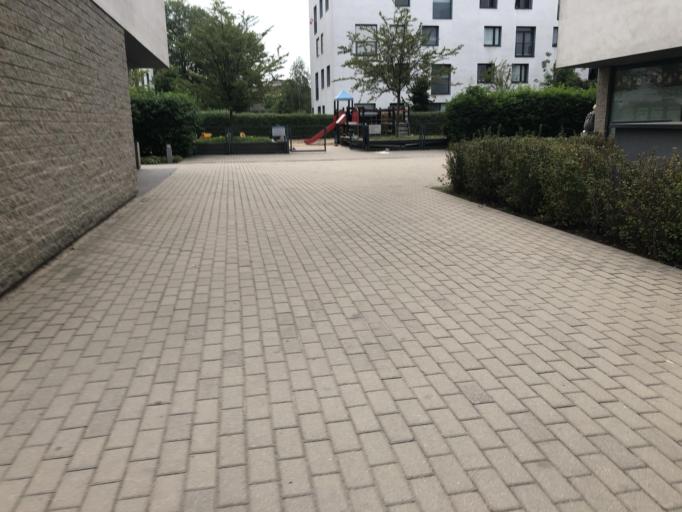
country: PL
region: Masovian Voivodeship
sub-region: Warszawa
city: Praga Poludnie
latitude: 52.2461
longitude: 21.1145
